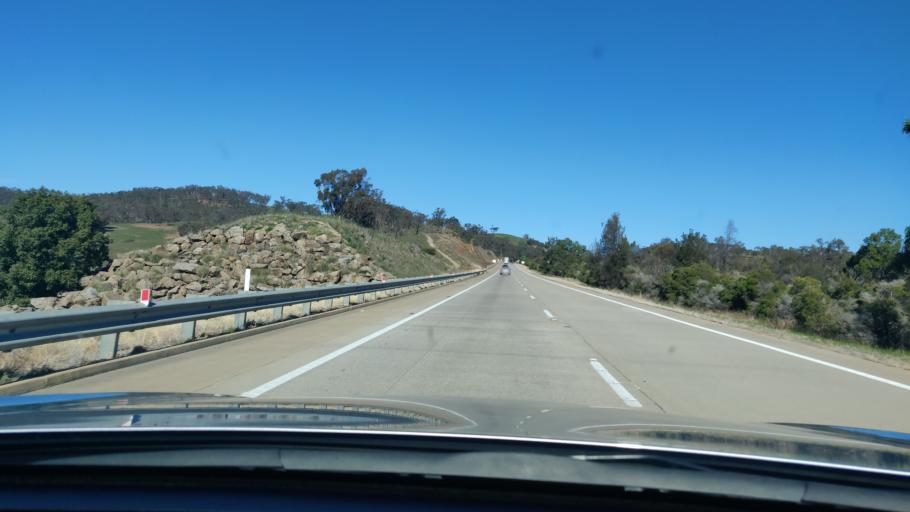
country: AU
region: New South Wales
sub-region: Gundagai
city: Gundagai
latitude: -35.2074
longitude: 147.8142
